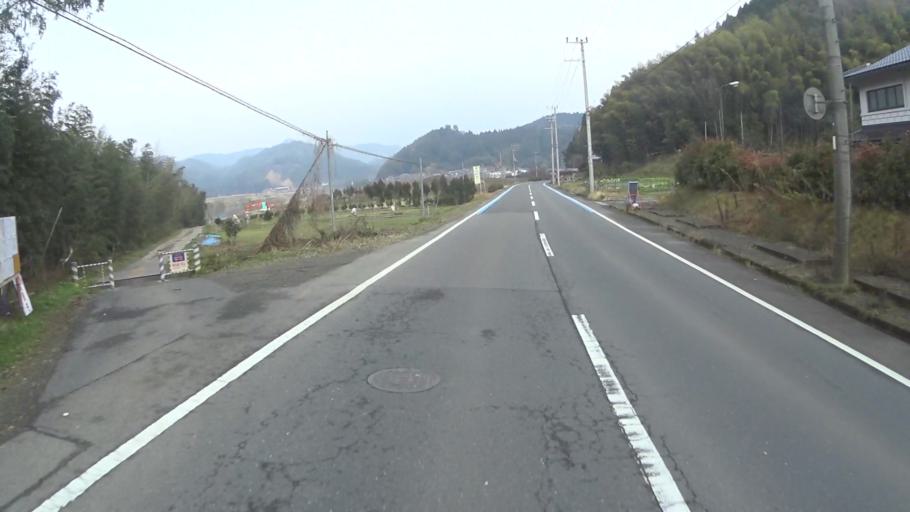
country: JP
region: Kyoto
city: Ayabe
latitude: 35.3935
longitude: 135.1856
